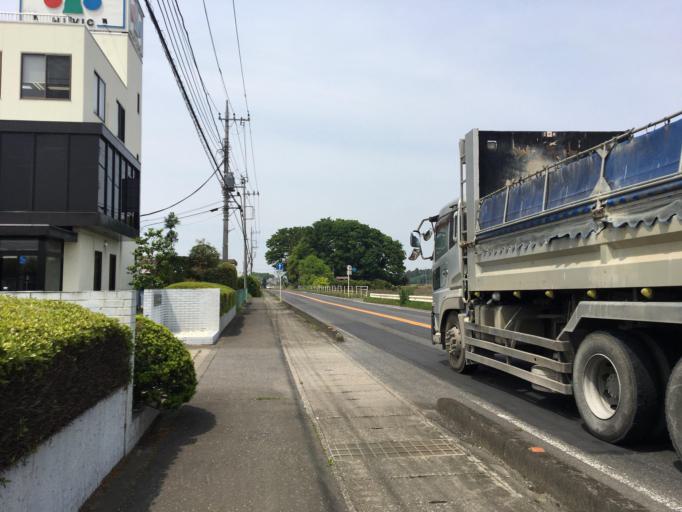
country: JP
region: Tochigi
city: Mibu
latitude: 36.3638
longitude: 139.8057
